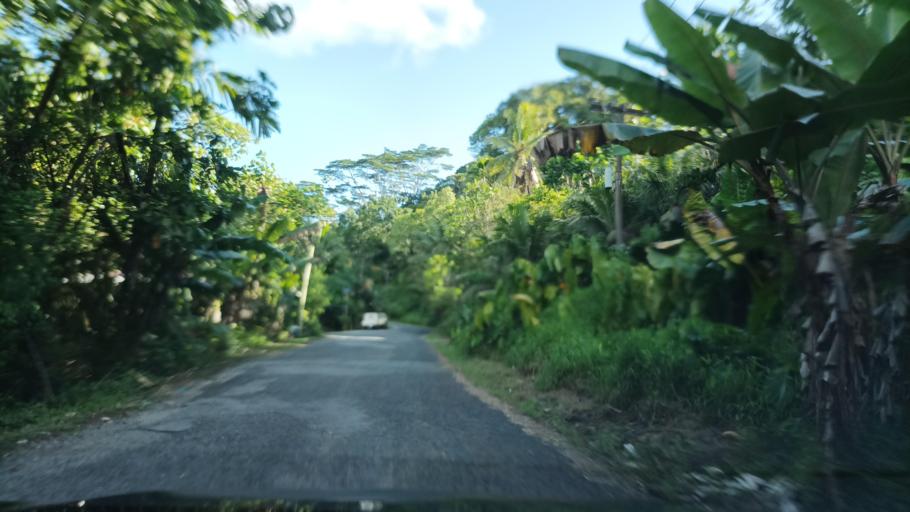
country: FM
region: Pohnpei
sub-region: Sokehs Municipality
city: Palikir - National Government Center
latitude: 6.8248
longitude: 158.1678
